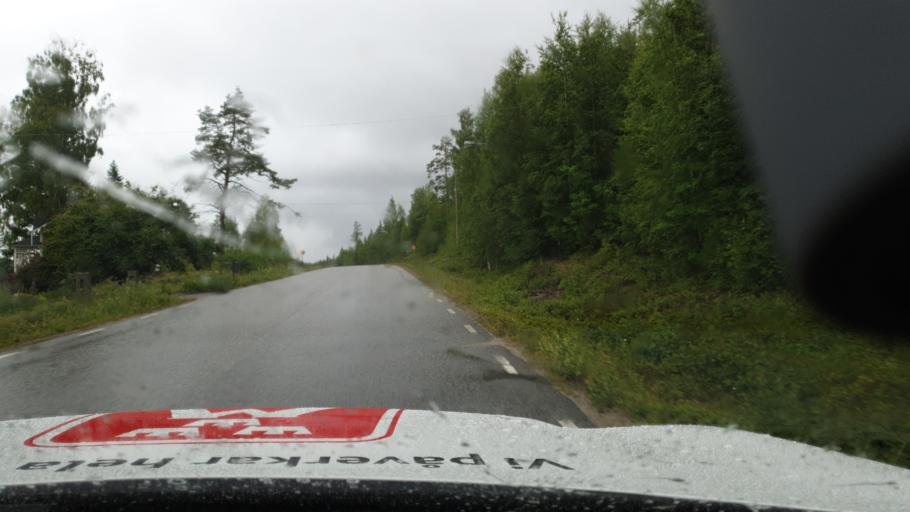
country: SE
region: Vaesterbotten
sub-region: Vindelns Kommun
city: Vindeln
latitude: 64.3164
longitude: 19.6270
